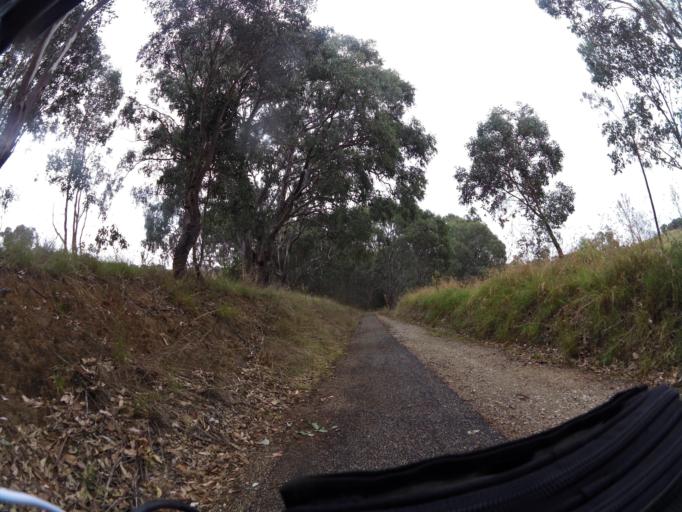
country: AU
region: New South Wales
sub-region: Albury Municipality
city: East Albury
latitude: -36.2252
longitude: 147.1269
